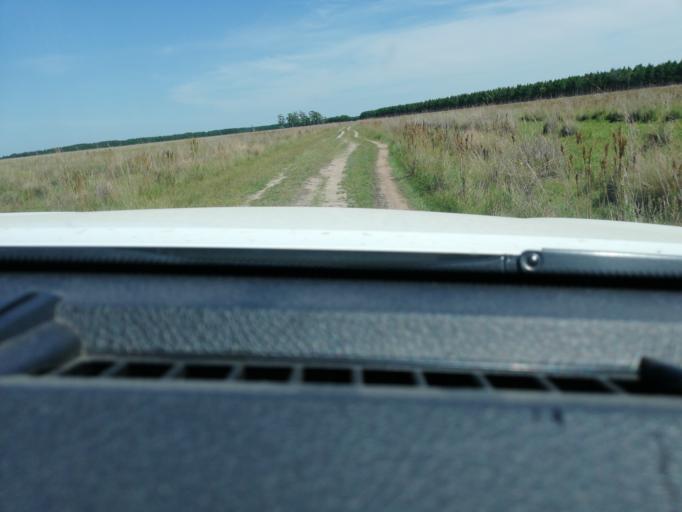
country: AR
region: Corrientes
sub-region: Departamento de San Miguel
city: San Miguel
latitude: -28.0420
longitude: -57.4593
